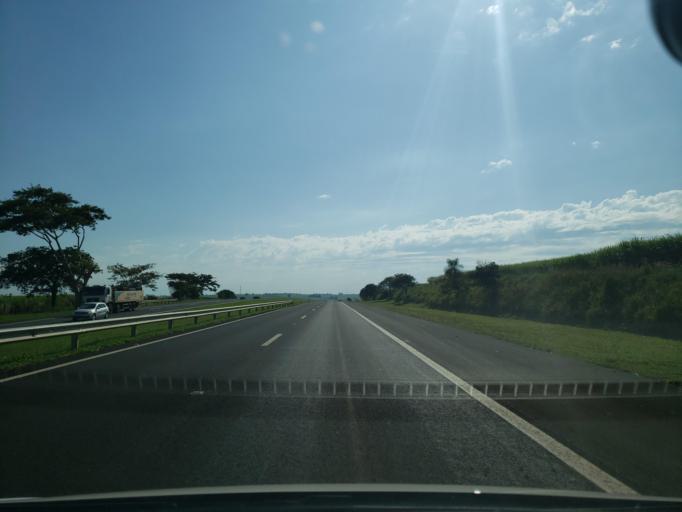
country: BR
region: Sao Paulo
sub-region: Promissao
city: Promissao
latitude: -21.5395
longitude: -49.9722
